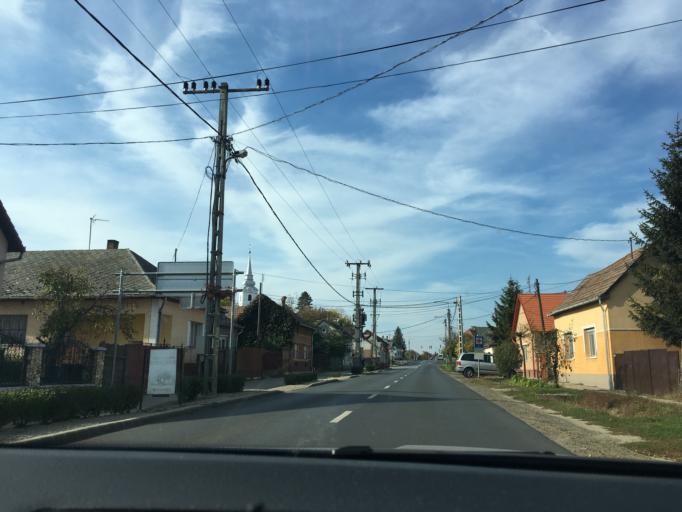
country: HU
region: Hajdu-Bihar
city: Vamospercs
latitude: 47.5254
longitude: 21.9011
